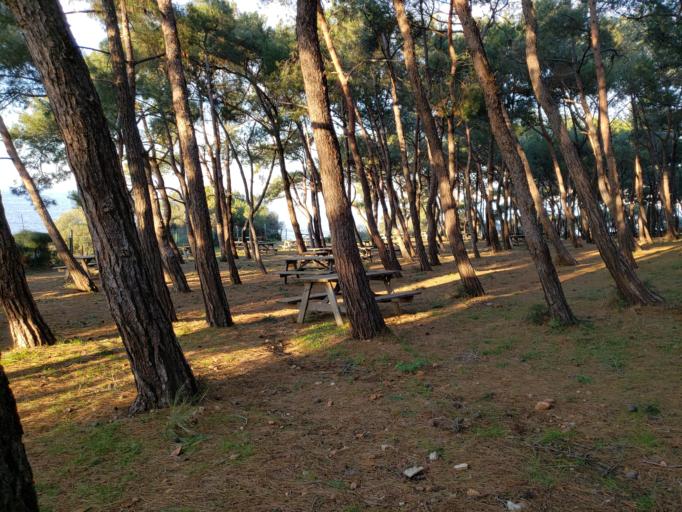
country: TR
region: Istanbul
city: Adalan
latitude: 40.8838
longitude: 29.0922
